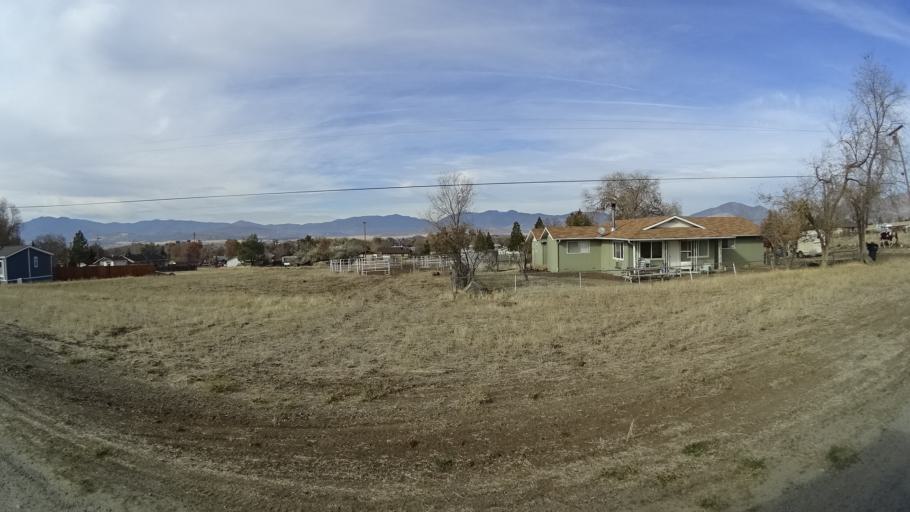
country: US
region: California
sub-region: Siskiyou County
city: Montague
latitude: 41.7282
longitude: -122.5155
